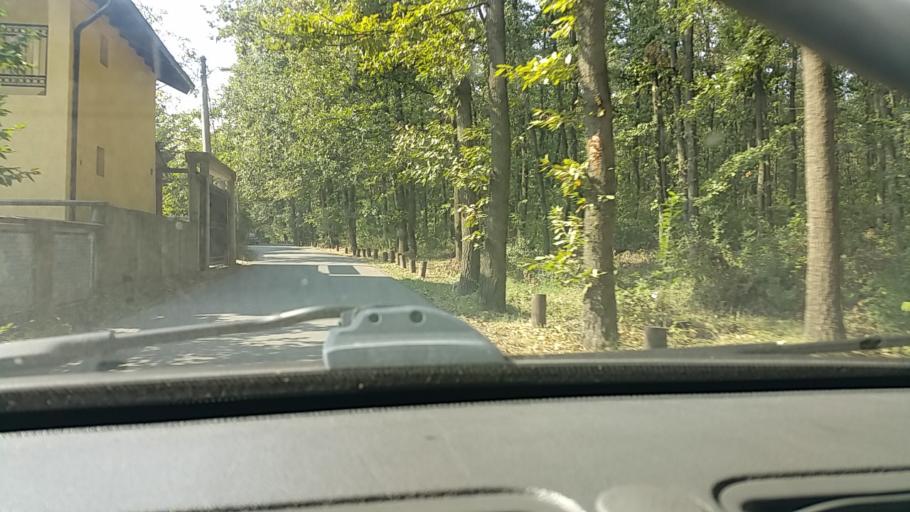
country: RS
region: Central Serbia
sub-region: Belgrade
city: Rakovica
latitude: 44.7393
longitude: 20.4602
